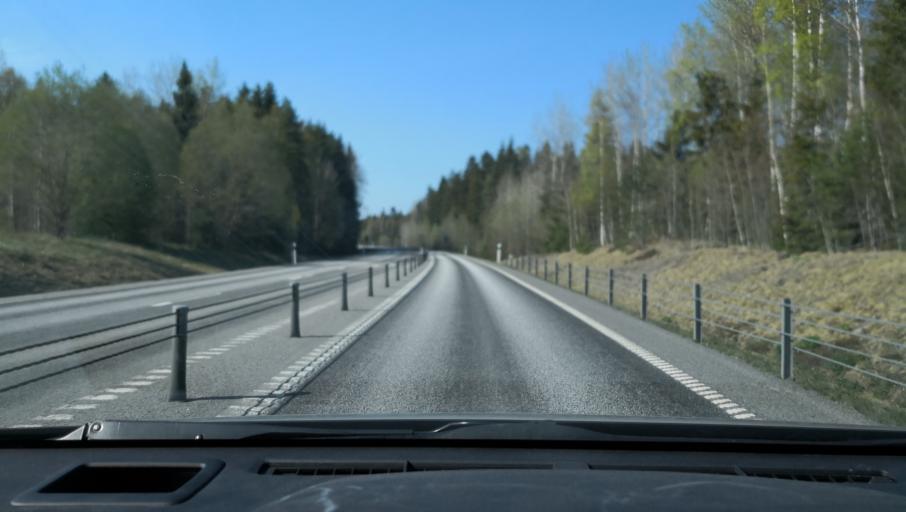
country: SE
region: Uppsala
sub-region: Heby Kommun
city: Tarnsjo
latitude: 60.1717
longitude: 16.9544
